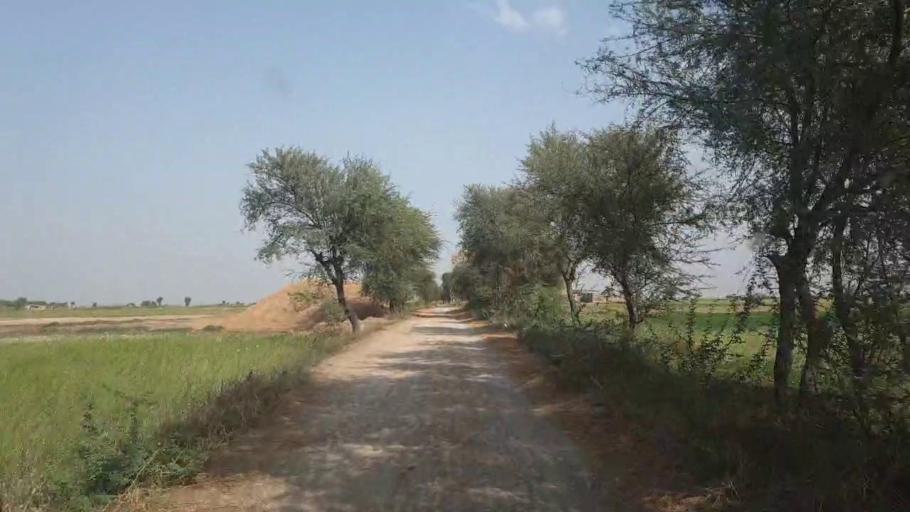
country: PK
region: Sindh
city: Kario
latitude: 24.5531
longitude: 68.5395
